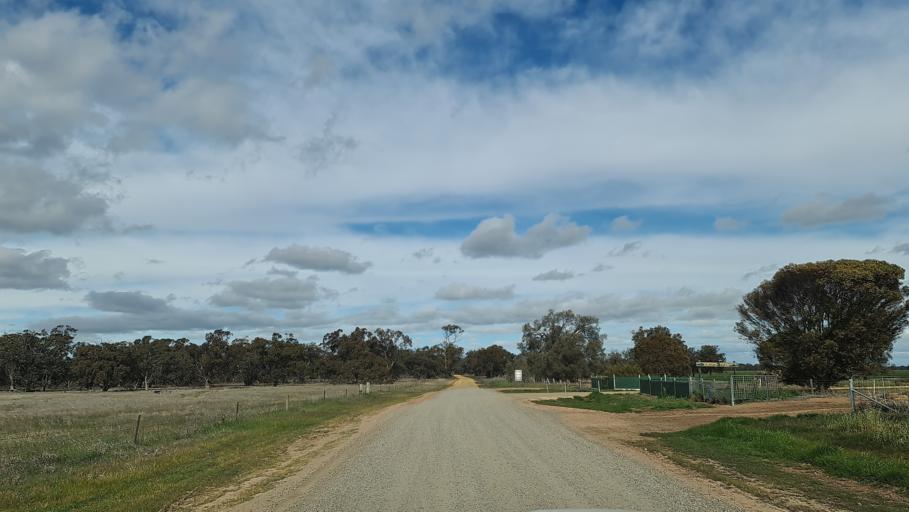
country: AU
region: Victoria
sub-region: Horsham
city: Horsham
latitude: -36.6316
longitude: 142.4117
